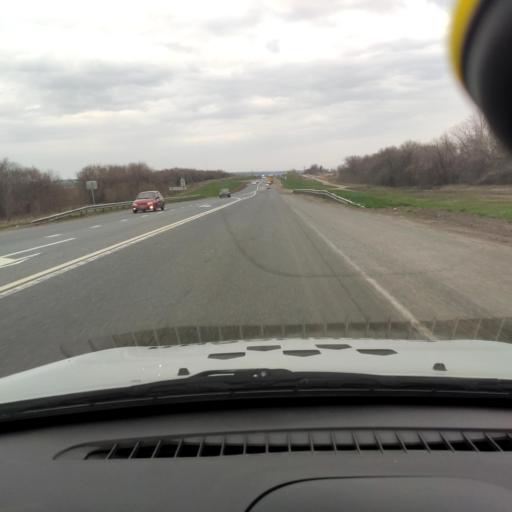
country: RU
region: Samara
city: Mezhdurechensk
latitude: 53.2547
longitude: 49.1404
